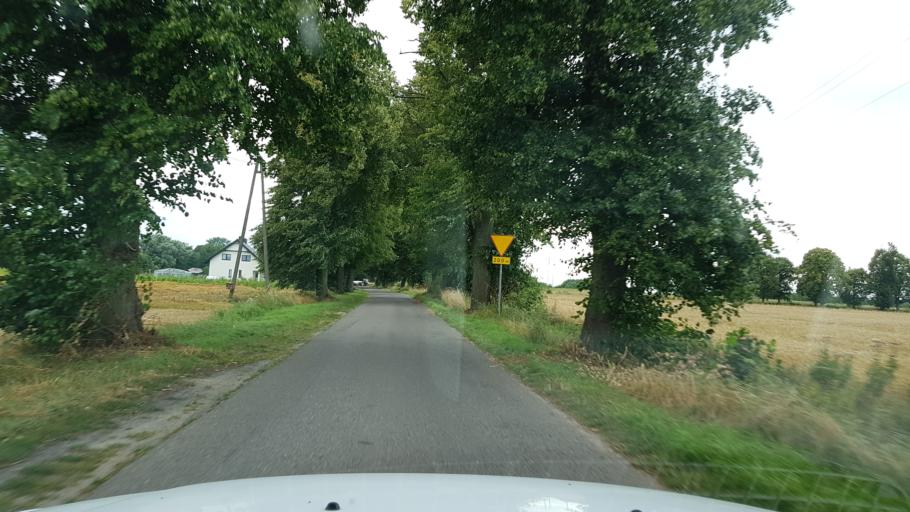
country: PL
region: West Pomeranian Voivodeship
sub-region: Powiat bialogardzki
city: Karlino
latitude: 54.1160
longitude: 15.8492
